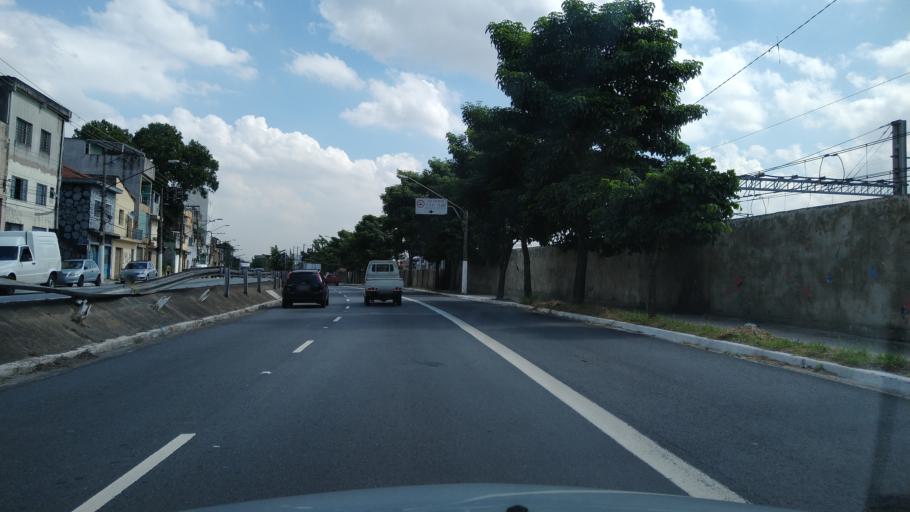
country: BR
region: Sao Paulo
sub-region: Guarulhos
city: Guarulhos
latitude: -23.5000
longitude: -46.5305
